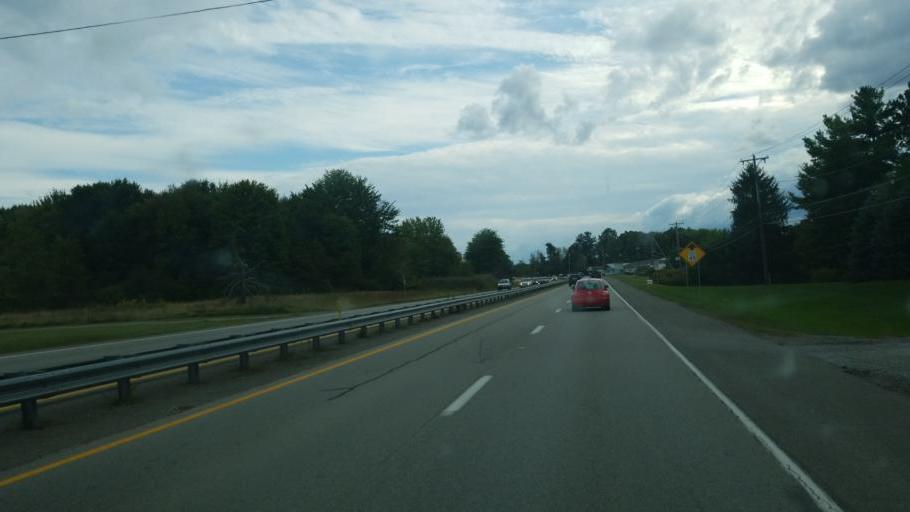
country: US
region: Pennsylvania
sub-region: Mercer County
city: Reynolds Heights
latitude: 41.3369
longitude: -80.4121
